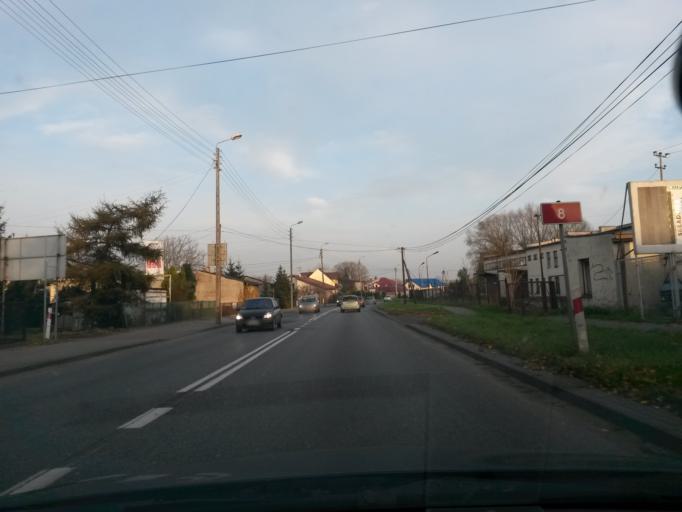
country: PL
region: Lodz Voivodeship
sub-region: Powiat wielunski
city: Wielun
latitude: 51.2254
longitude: 18.5649
